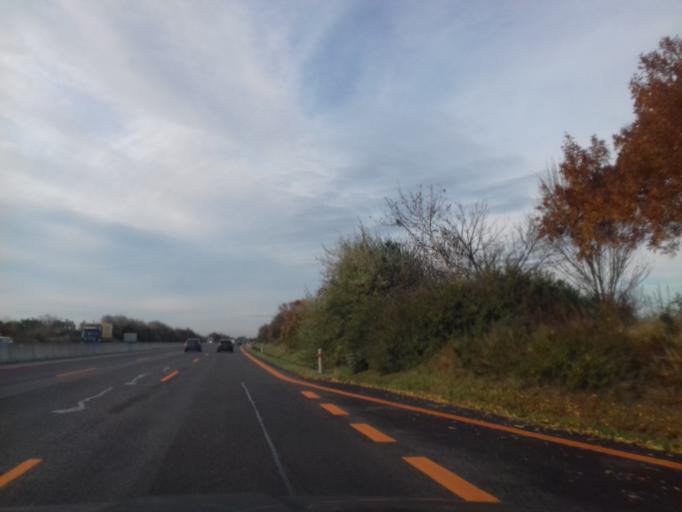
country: SK
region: Bratislavsky
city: Senec
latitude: 48.2228
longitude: 17.3435
